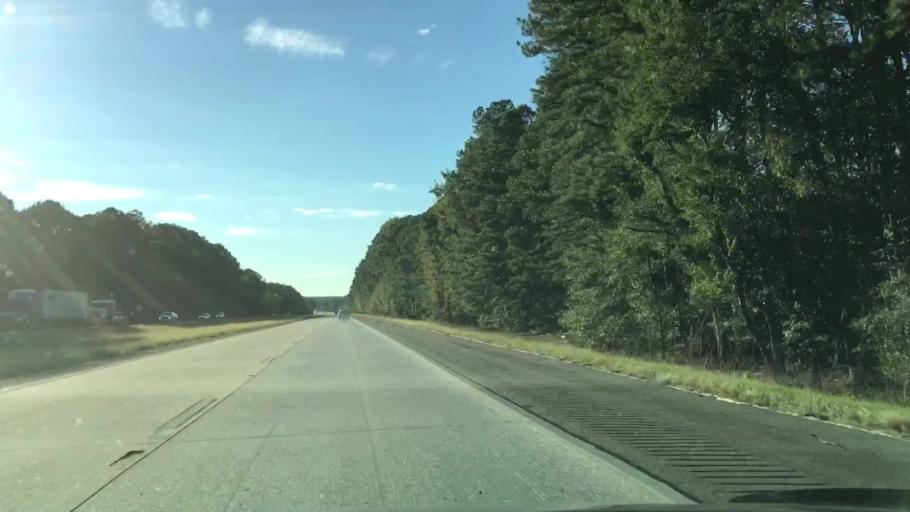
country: US
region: Georgia
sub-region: Greene County
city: Greensboro
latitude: 33.5478
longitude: -83.1153
